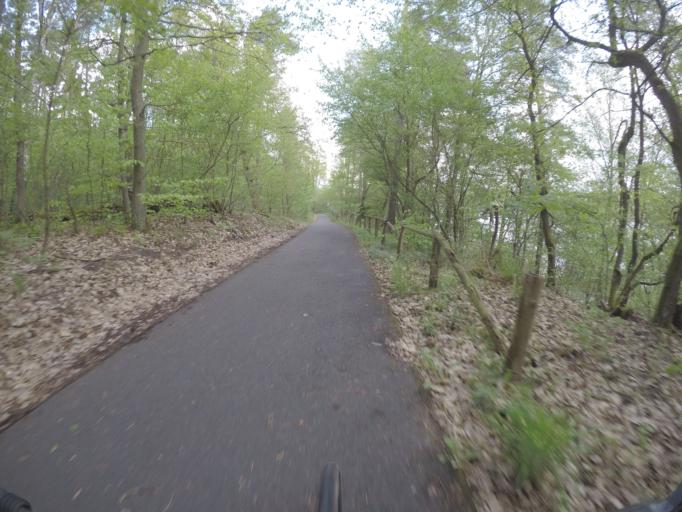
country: DE
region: Brandenburg
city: Joachimsthal
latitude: 52.9389
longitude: 13.7157
